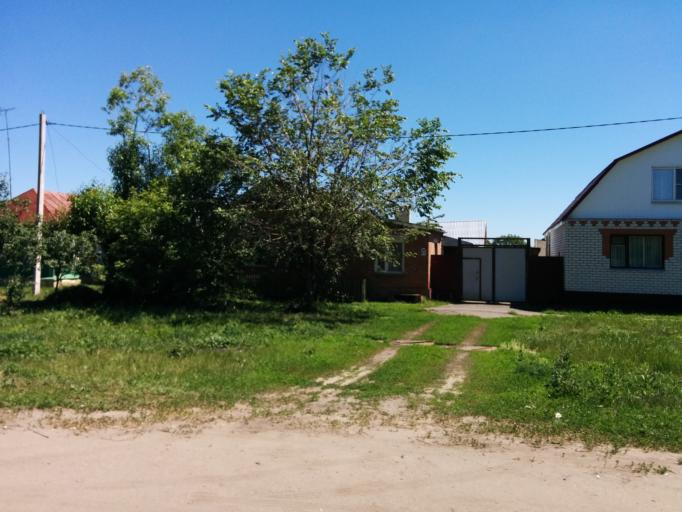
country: RU
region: Tambov
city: Morshansk
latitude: 53.3887
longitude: 41.7790
